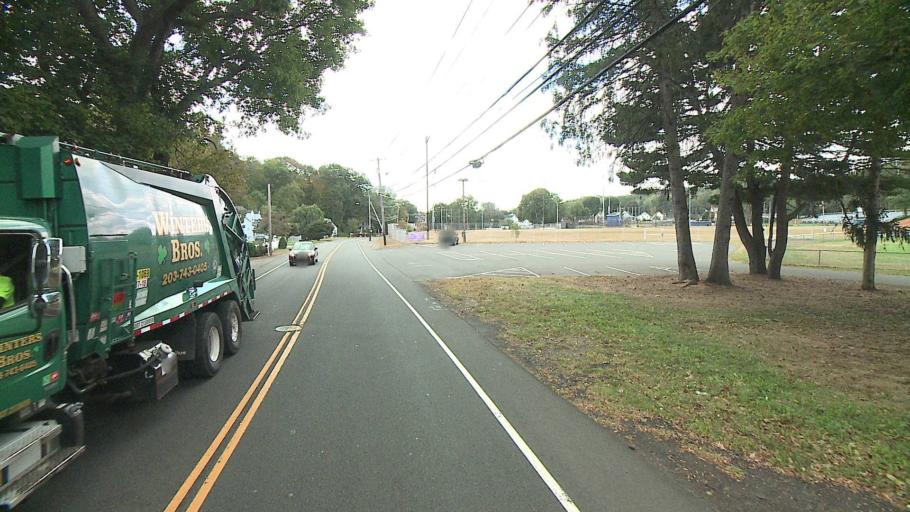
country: US
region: Connecticut
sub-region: New Haven County
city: Ansonia
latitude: 41.3557
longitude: -73.0913
